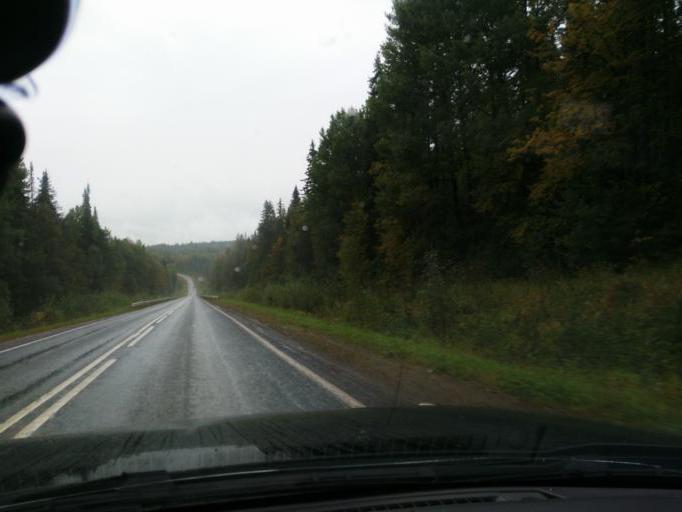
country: RU
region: Perm
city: Yugo-Kamskiy
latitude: 57.5883
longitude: 55.6701
